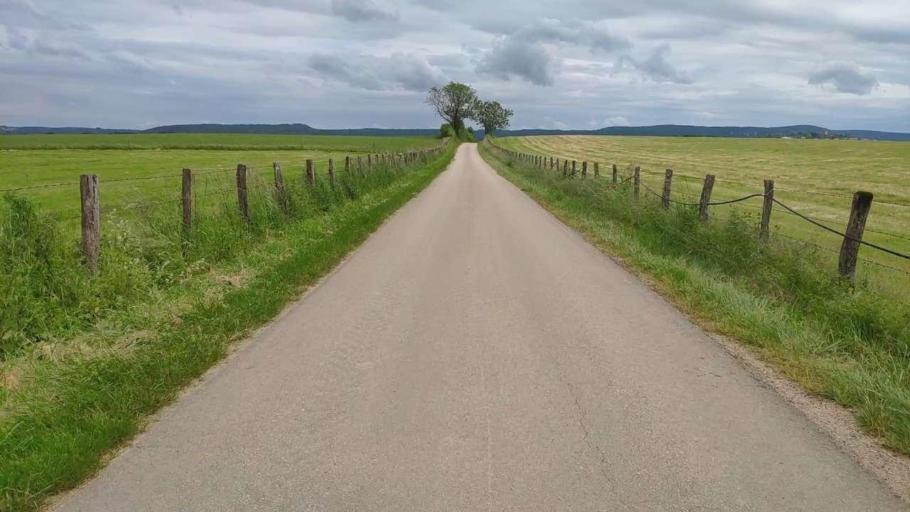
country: FR
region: Franche-Comte
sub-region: Departement du Jura
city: Montmorot
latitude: 46.7440
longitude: 5.5525
